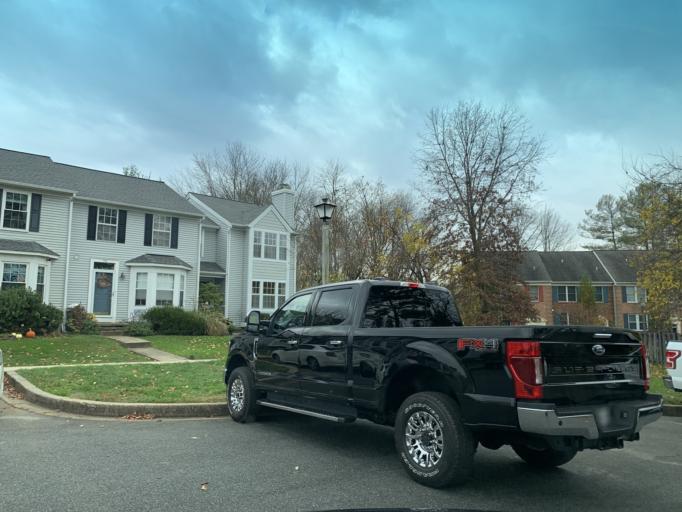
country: US
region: Maryland
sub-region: Harford County
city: North Bel Air
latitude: 39.5478
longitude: -76.3480
